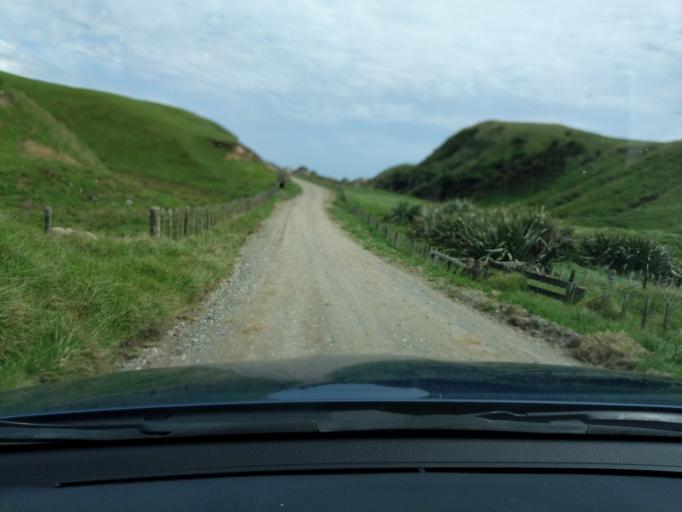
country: NZ
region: Tasman
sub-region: Tasman District
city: Takaka
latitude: -40.6524
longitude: 172.4205
